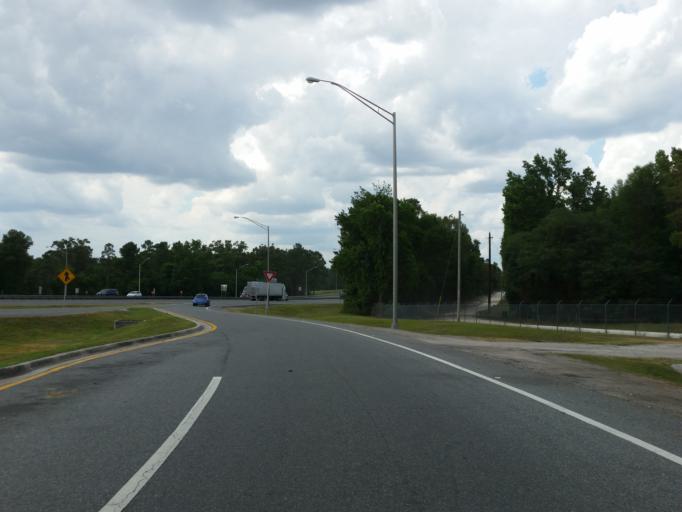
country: US
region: Florida
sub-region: Alachua County
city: High Springs
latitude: 29.9790
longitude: -82.5782
